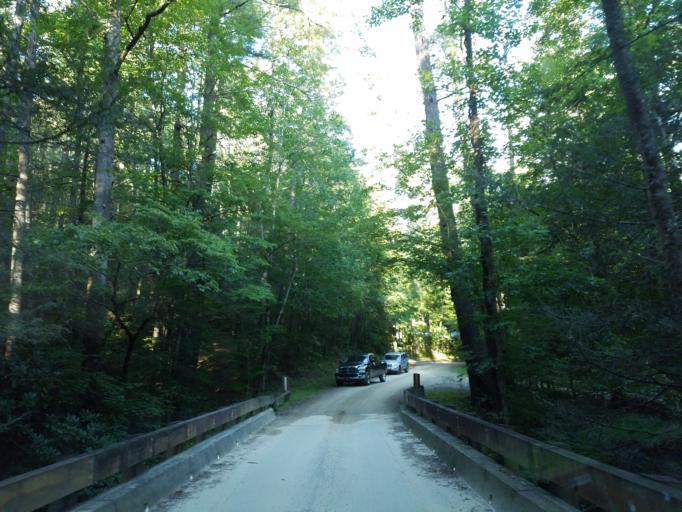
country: US
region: Georgia
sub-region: Union County
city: Blairsville
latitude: 34.7642
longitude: -84.0687
